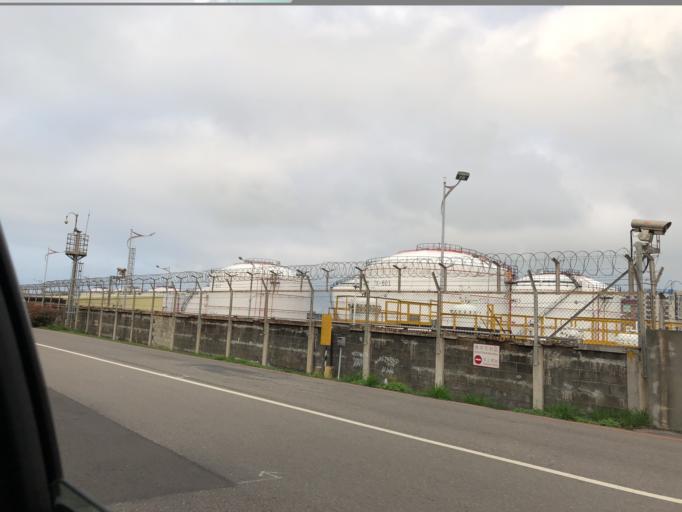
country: TW
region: Taiwan
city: Taoyuan City
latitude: 25.0898
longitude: 121.2499
